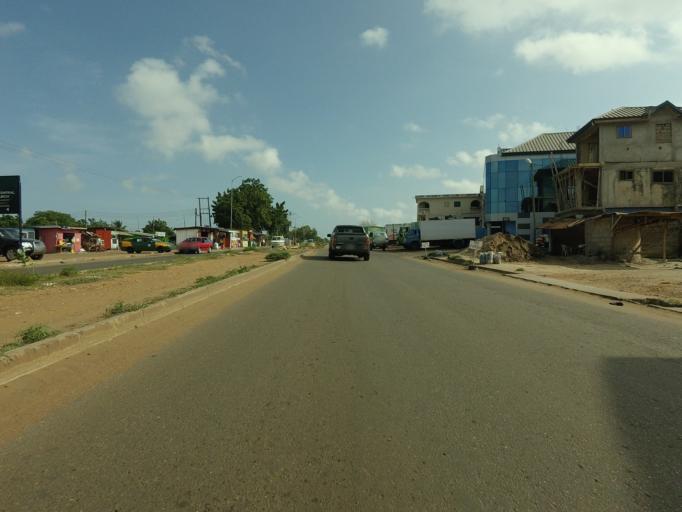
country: GH
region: Greater Accra
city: Tema
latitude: 5.6651
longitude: -0.0493
